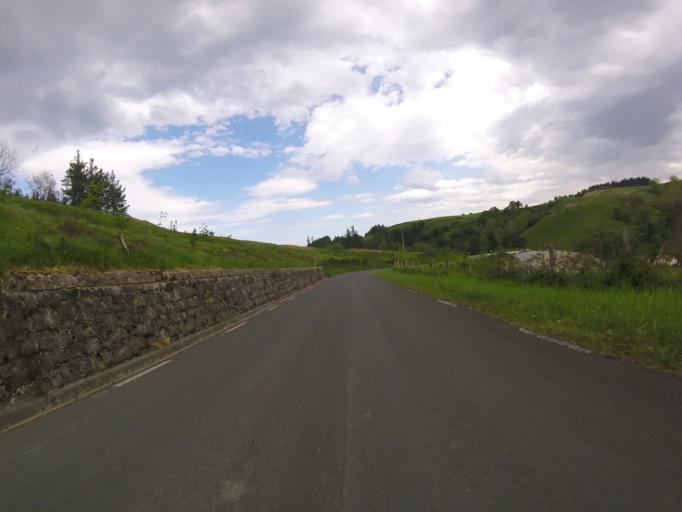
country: ES
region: Basque Country
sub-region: Provincia de Guipuzcoa
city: Zarautz
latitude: 43.2688
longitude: -2.1672
